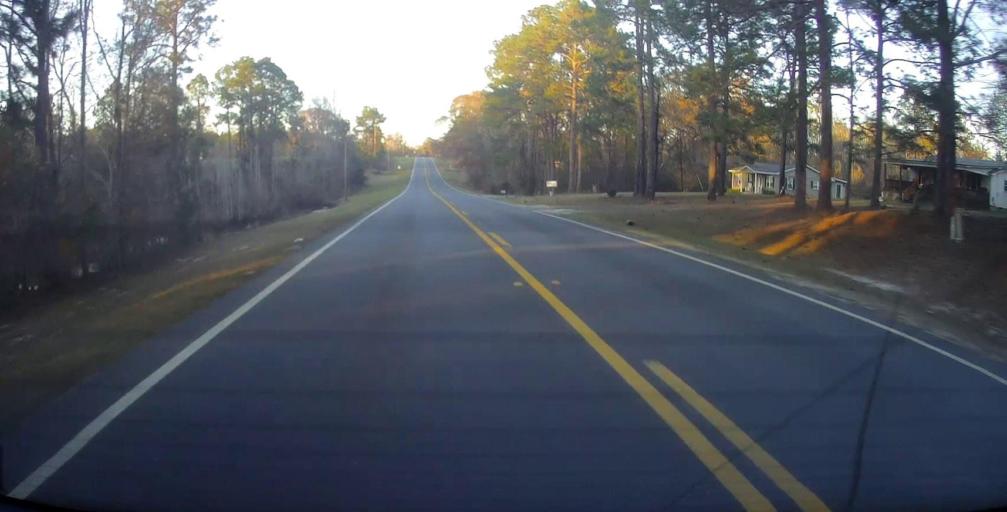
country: US
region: Georgia
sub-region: Dodge County
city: Chester
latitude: 32.3328
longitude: -83.0464
